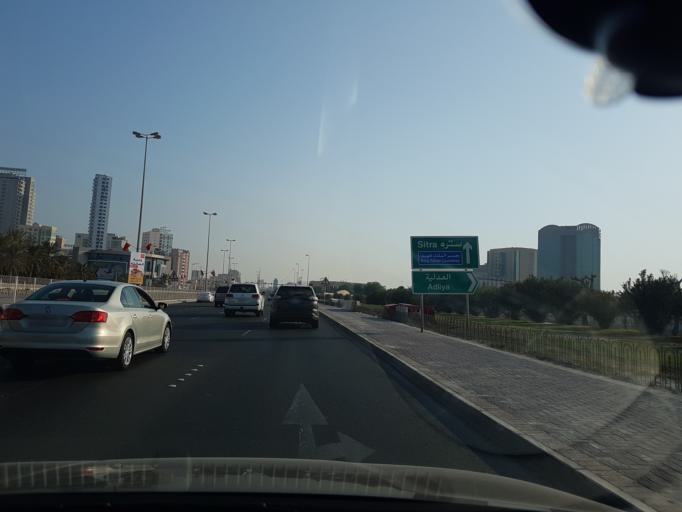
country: BH
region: Manama
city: Manama
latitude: 26.2196
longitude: 50.5971
